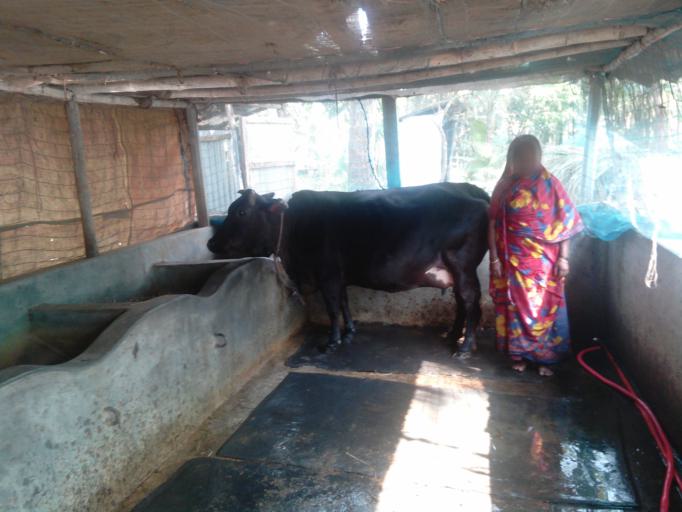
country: BD
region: Khulna
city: Kesabpur
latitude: 22.7849
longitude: 89.2786
